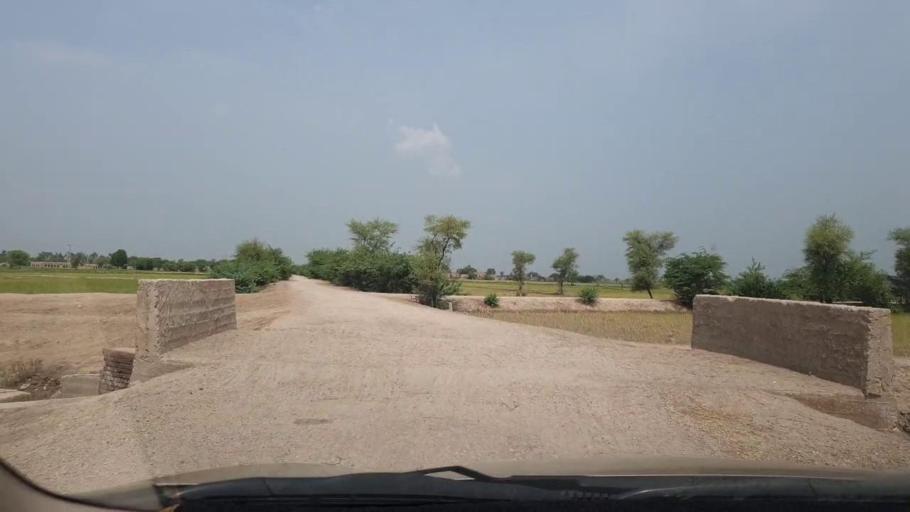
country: PK
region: Sindh
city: Larkana
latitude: 27.5080
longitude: 68.1372
